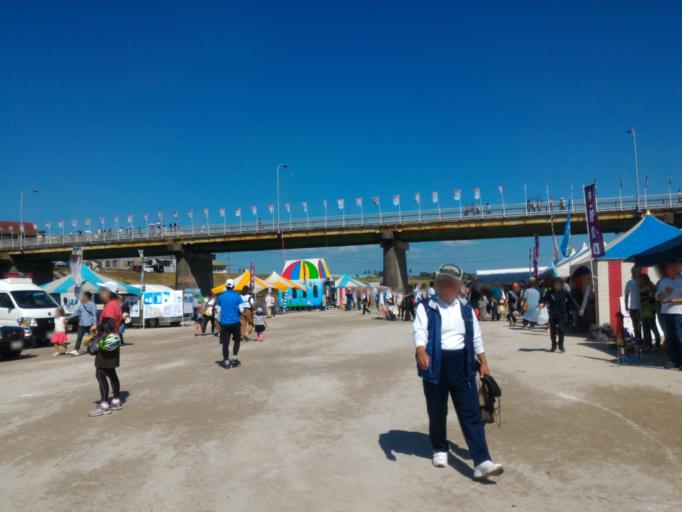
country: JP
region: Kagoshima
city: Kanoya
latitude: 31.3460
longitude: 130.9427
